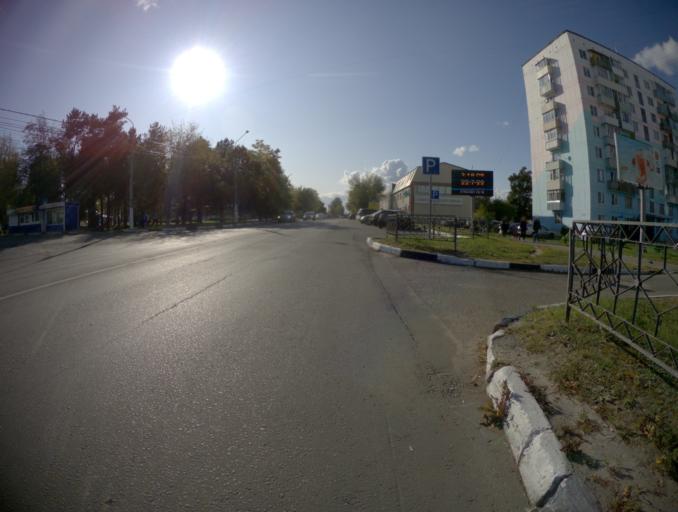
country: RU
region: Moskovskaya
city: Shatura
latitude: 55.5757
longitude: 39.5268
